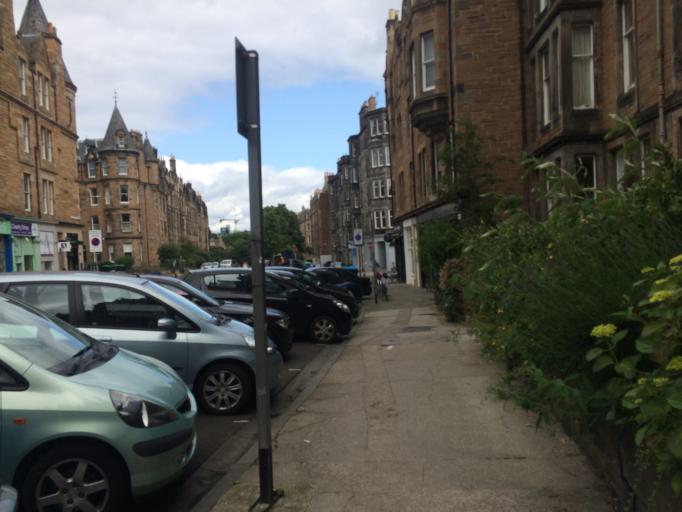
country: GB
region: Scotland
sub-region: Edinburgh
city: Edinburgh
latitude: 55.9376
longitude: -3.1931
